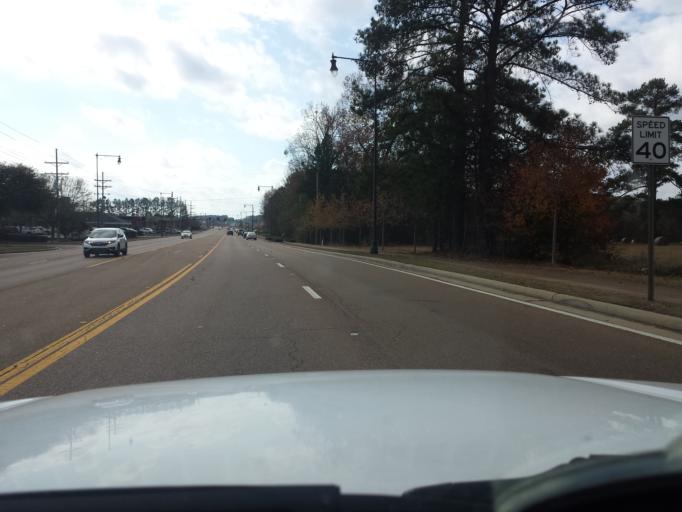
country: US
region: Mississippi
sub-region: Rankin County
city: Flowood
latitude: 32.3484
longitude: -90.0648
